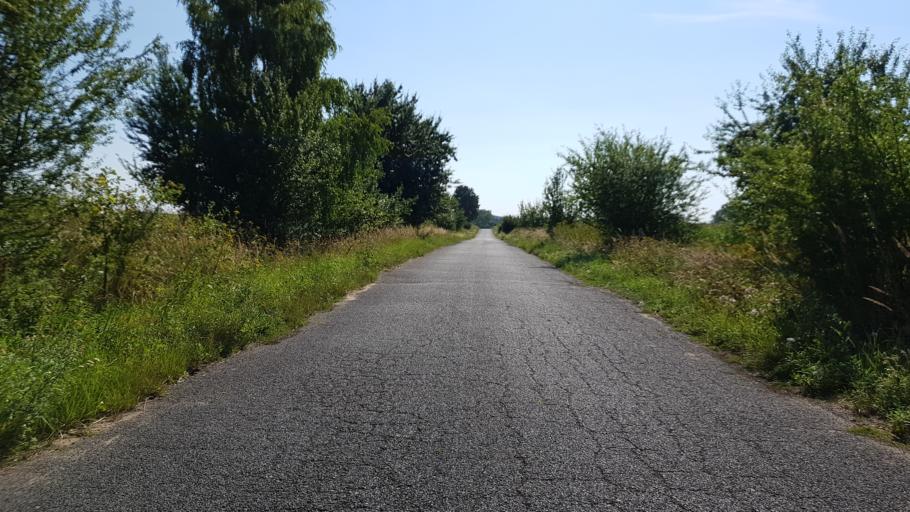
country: PL
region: West Pomeranian Voivodeship
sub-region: Powiat gryfinski
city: Gryfino
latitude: 53.1535
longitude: 14.5187
